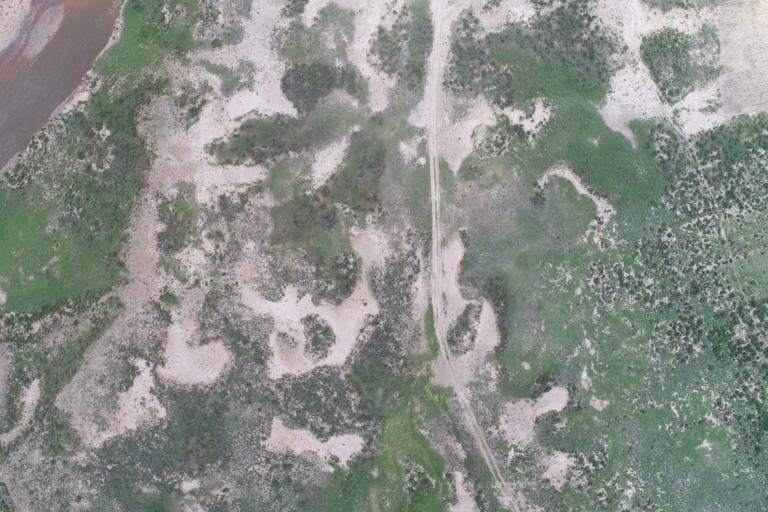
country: BO
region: La Paz
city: Curahuara de Carangas
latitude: -17.3195
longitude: -68.5105
